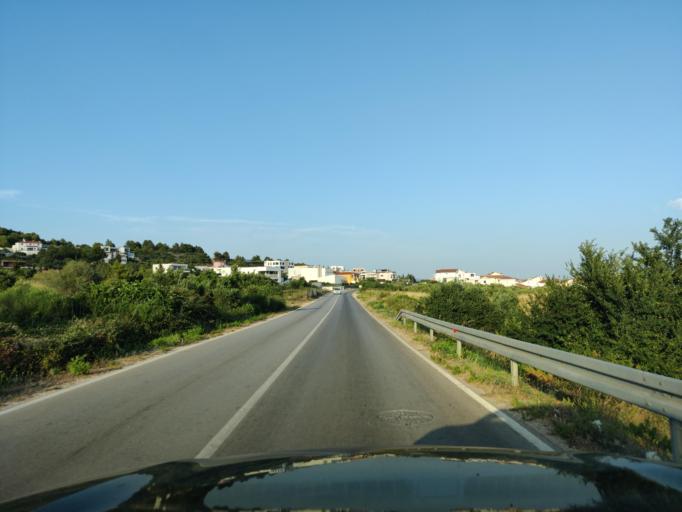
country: HR
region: Sibensko-Kniniska
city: Tribunj
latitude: 43.7589
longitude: 15.7565
